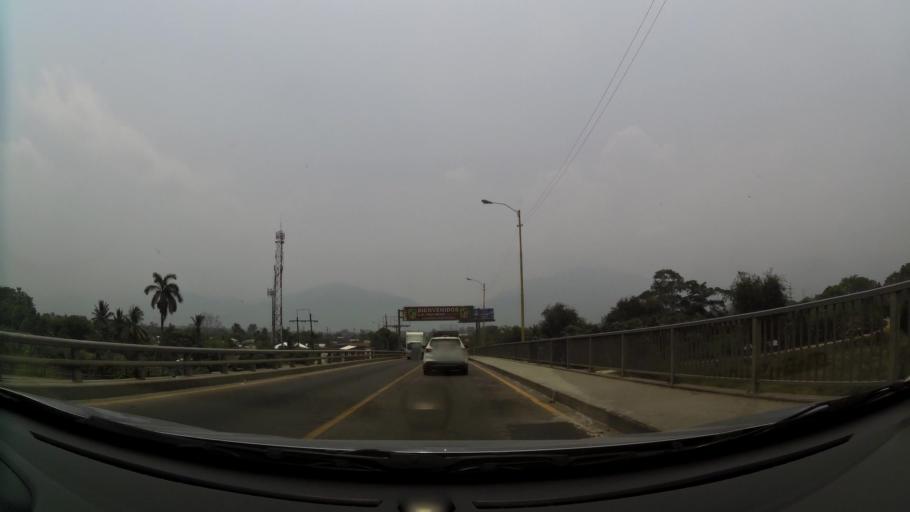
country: HN
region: Yoro
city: El Progreso
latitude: 15.4038
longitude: -87.8196
